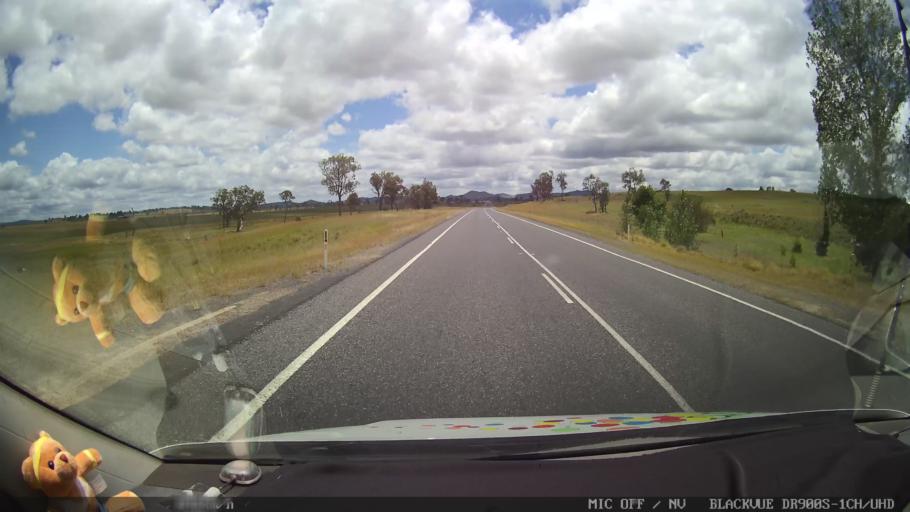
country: AU
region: New South Wales
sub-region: Glen Innes Severn
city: Glen Innes
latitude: -29.4140
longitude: 151.8656
